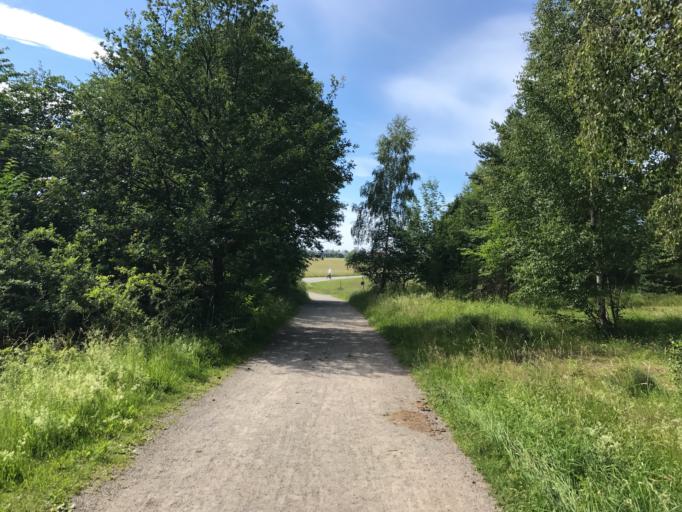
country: SE
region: Stockholm
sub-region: Lidingo
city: Lidingoe
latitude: 59.3342
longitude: 18.1236
